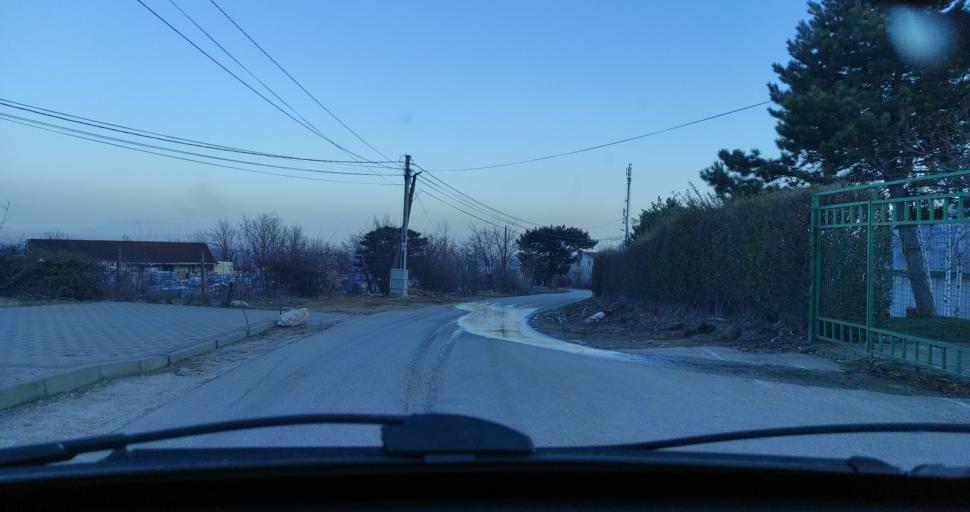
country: XK
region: Gjakova
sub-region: Komuna e Decanit
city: Decan
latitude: 42.5390
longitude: 20.2828
